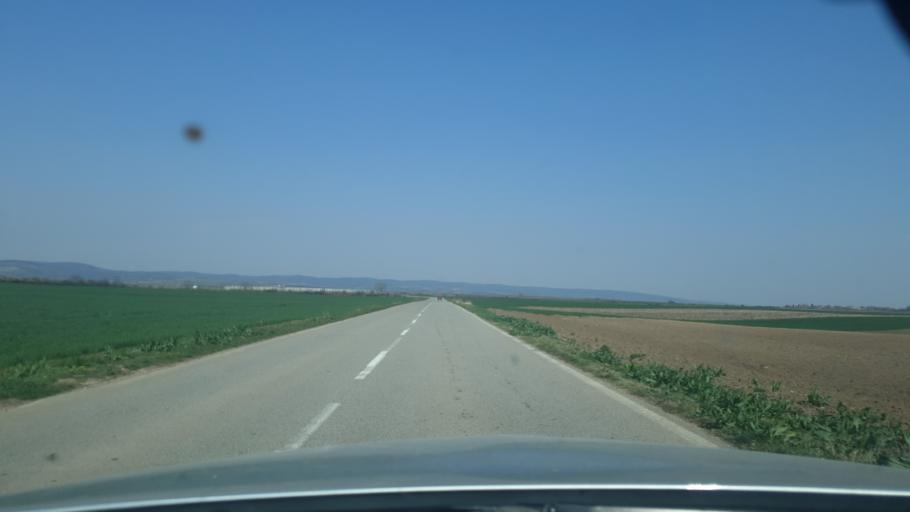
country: RS
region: Autonomna Pokrajina Vojvodina
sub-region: Sremski Okrug
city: Ruma
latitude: 45.0462
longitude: 19.7623
